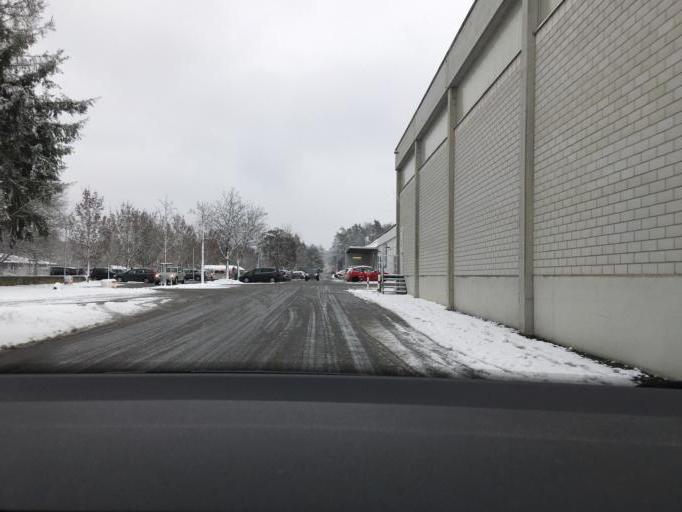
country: DE
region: Baden-Wuerttemberg
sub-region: Freiburg Region
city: Moos
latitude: 47.7621
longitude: 8.8918
